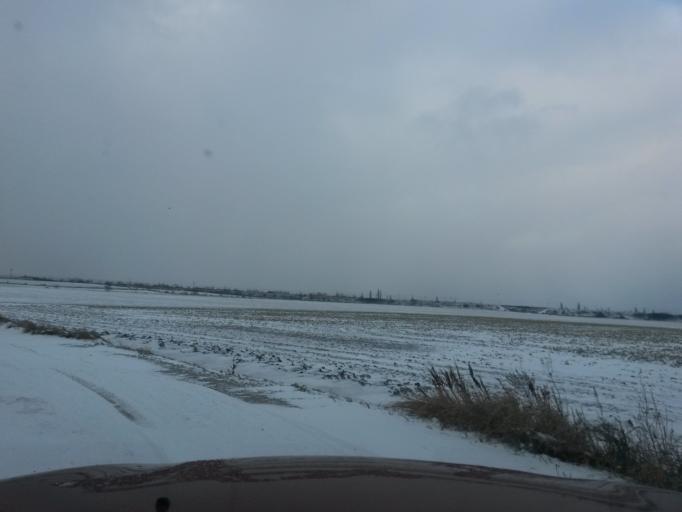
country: SK
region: Kosicky
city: Kosice
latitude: 48.6319
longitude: 21.2736
